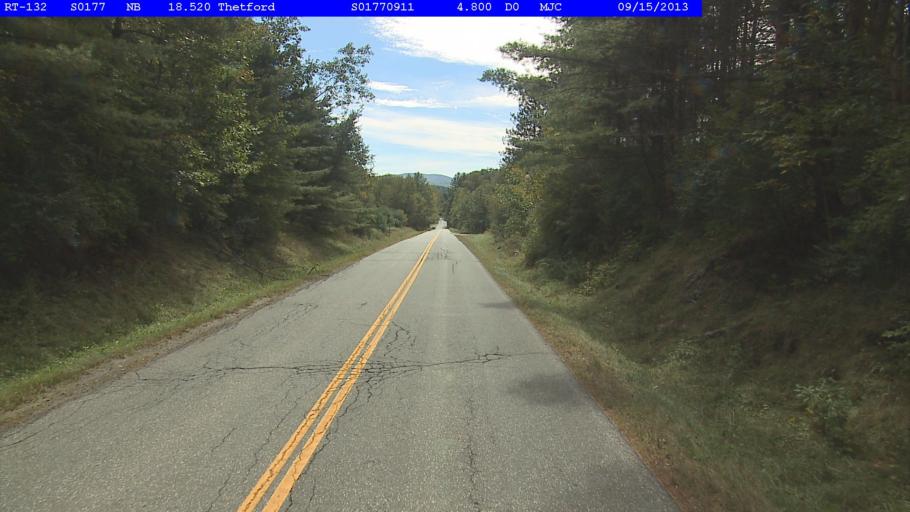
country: US
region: New Hampshire
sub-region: Grafton County
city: Hanover
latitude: 43.7913
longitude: -72.2624
